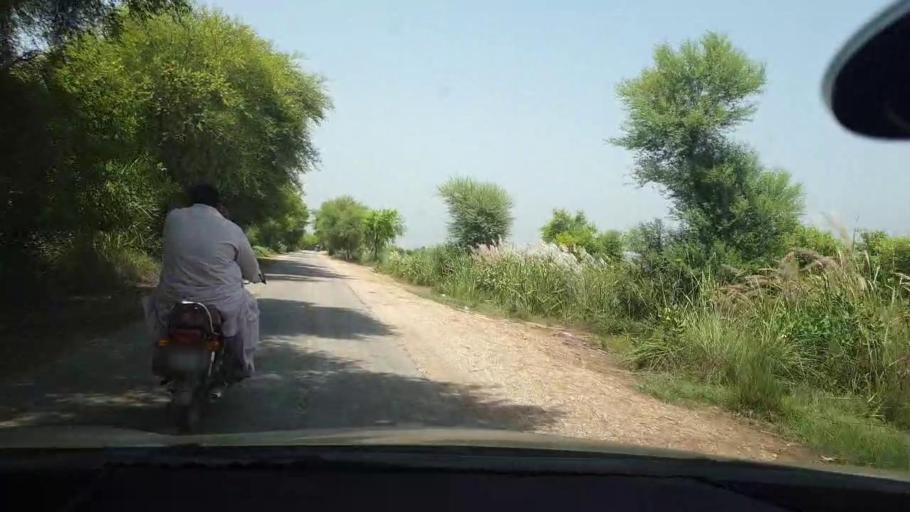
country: PK
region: Sindh
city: Kambar
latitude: 27.6389
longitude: 67.9765
